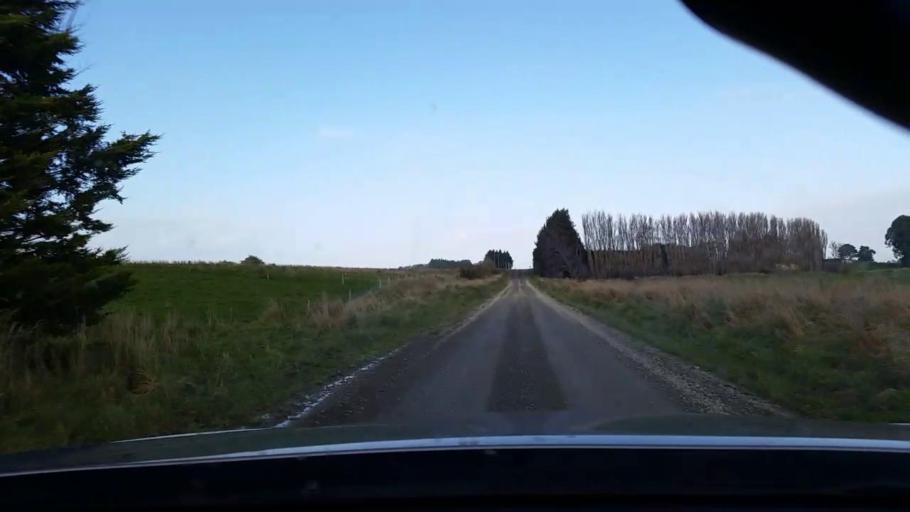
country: NZ
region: Southland
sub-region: Southland District
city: Winton
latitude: -46.2752
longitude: 168.2925
